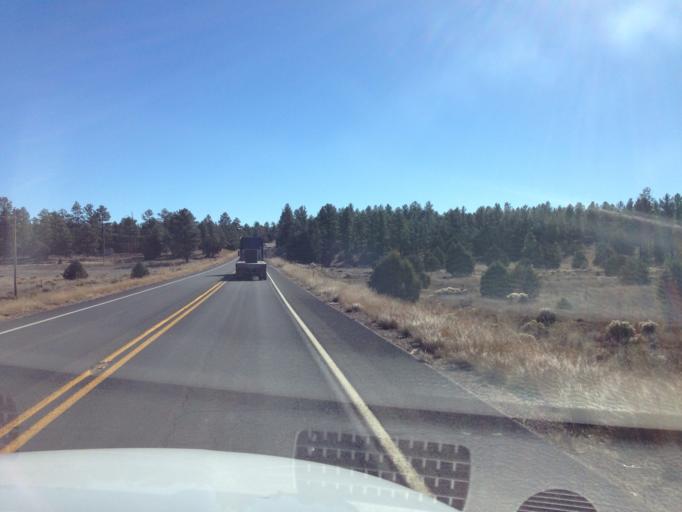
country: US
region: Arizona
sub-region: Navajo County
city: Linden
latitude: 34.2818
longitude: -110.1019
